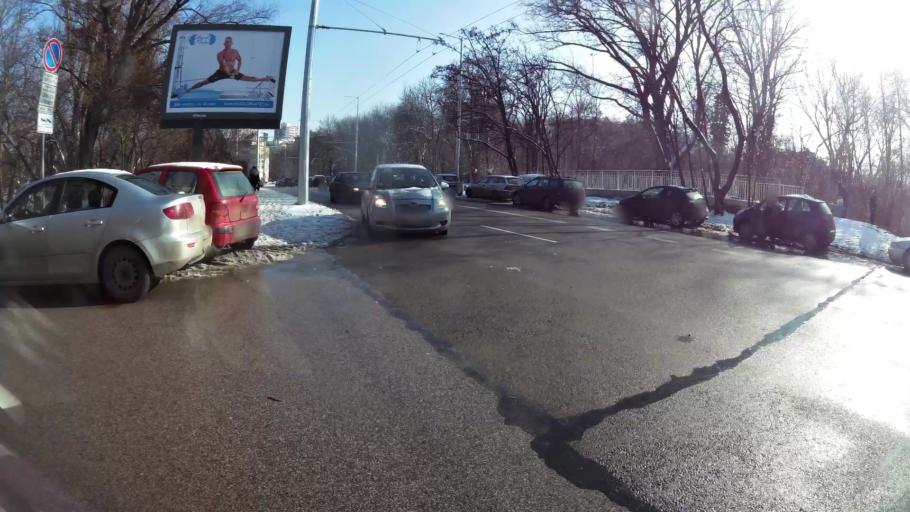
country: BG
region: Sofia-Capital
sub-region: Stolichna Obshtina
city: Sofia
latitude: 42.6746
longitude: 23.3099
